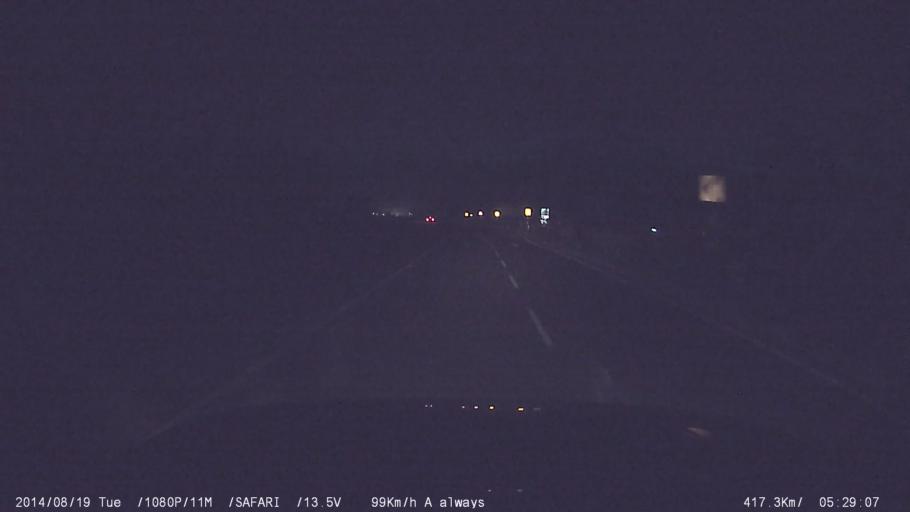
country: IN
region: Tamil Nadu
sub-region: Salem
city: Attayyampatti
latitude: 11.5975
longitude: 78.0865
